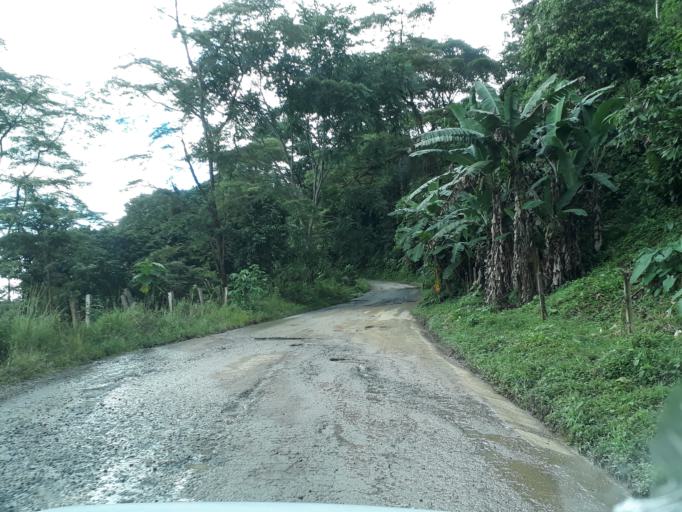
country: CO
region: Cundinamarca
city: Medina
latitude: 4.5641
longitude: -73.3637
